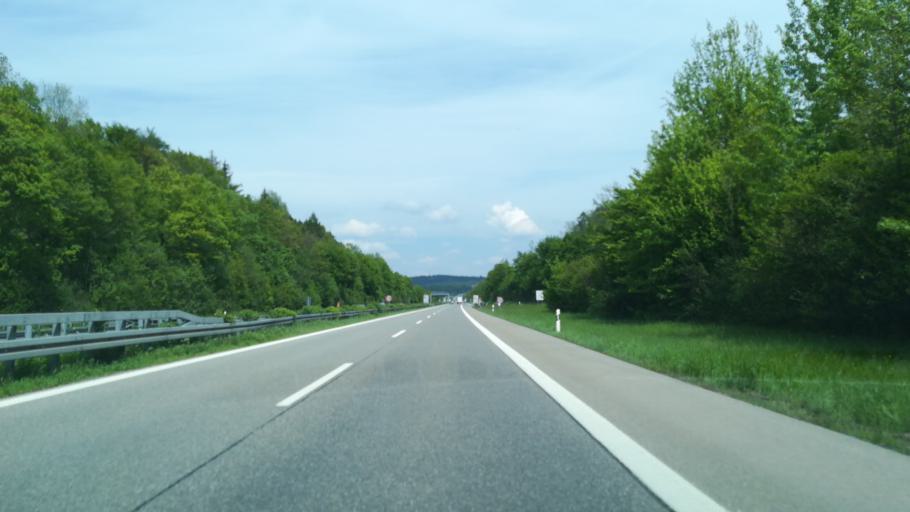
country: DE
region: Baden-Wuerttemberg
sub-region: Freiburg Region
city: Volkertshausen
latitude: 47.8103
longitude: 8.8651
